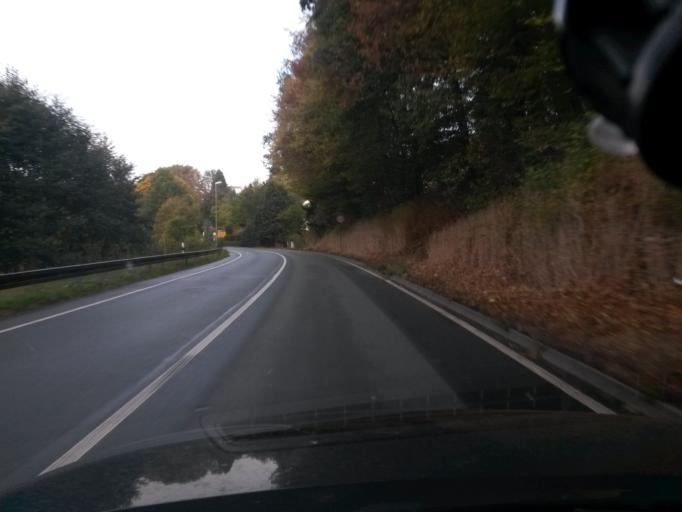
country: DE
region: North Rhine-Westphalia
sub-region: Regierungsbezirk Arnsberg
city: Luedenscheid
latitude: 51.2315
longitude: 7.6875
